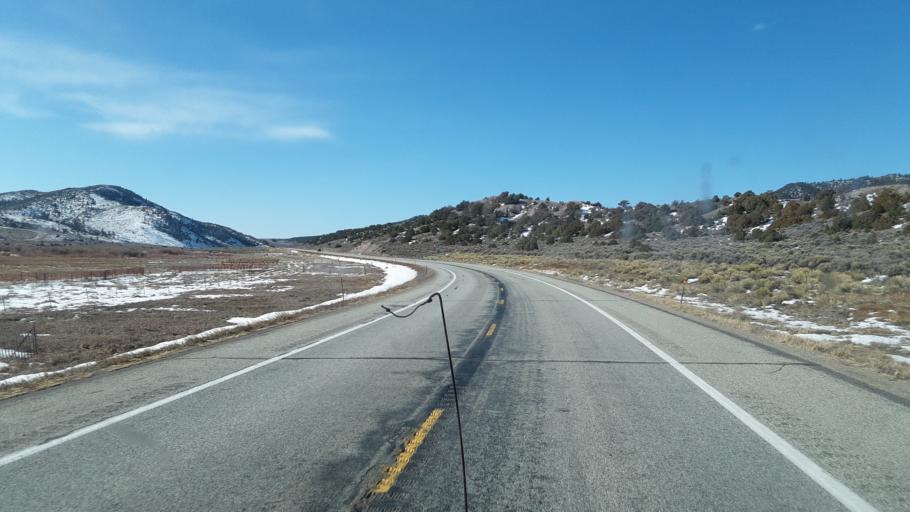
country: US
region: Colorado
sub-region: Costilla County
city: San Luis
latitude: 37.5145
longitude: -105.3108
